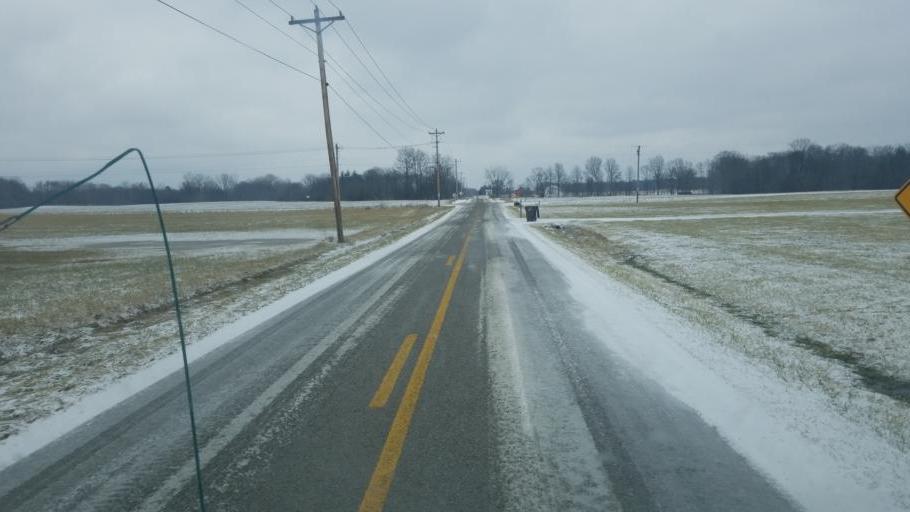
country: US
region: Ohio
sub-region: Knox County
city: Centerburg
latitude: 40.3089
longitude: -82.7737
